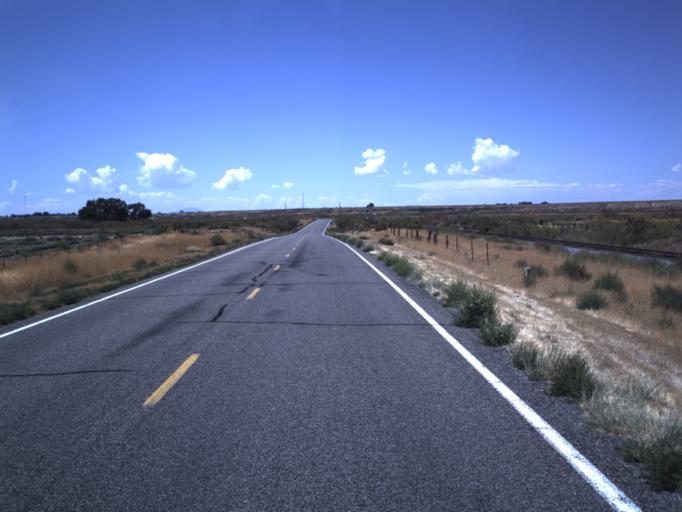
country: US
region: Utah
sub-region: Millard County
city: Delta
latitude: 39.5333
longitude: -112.3190
